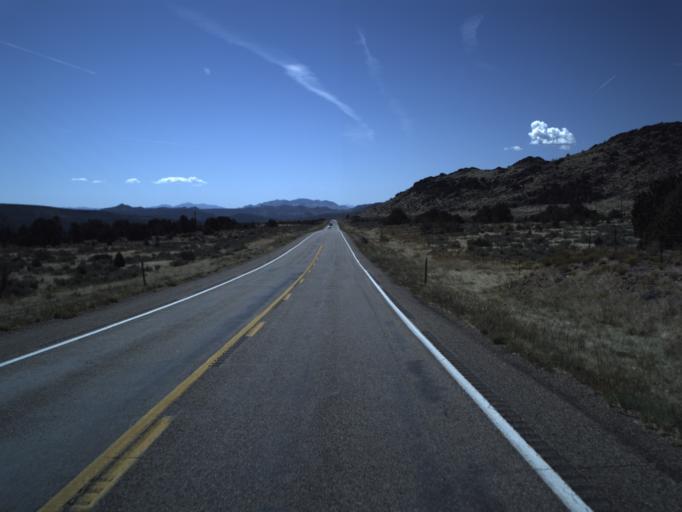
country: US
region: Utah
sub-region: Washington County
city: Enterprise
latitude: 37.3903
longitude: -113.6476
